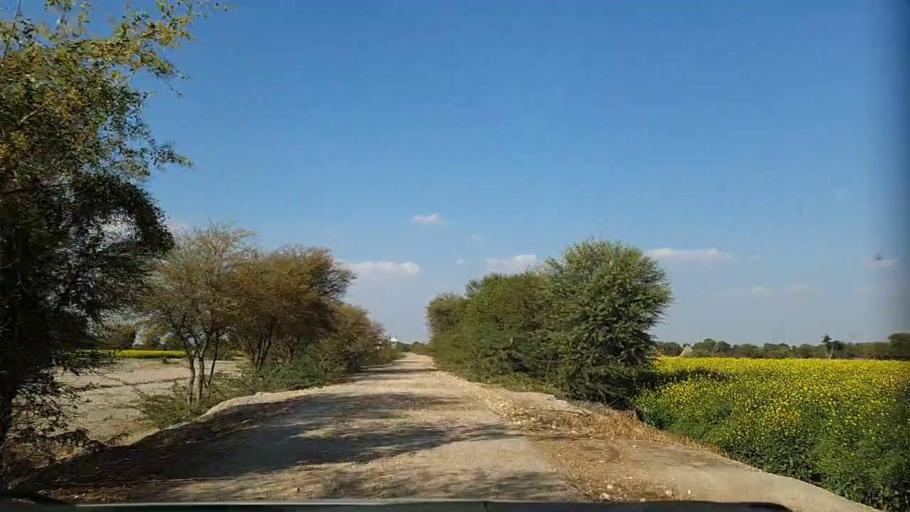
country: PK
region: Sindh
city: Pithoro
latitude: 25.6318
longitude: 69.3516
